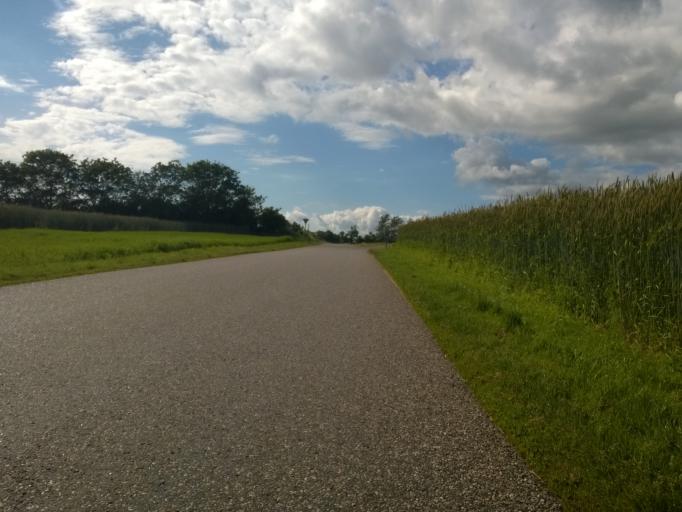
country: DK
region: Central Jutland
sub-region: Holstebro Kommune
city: Vinderup
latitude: 56.4740
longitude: 8.8591
